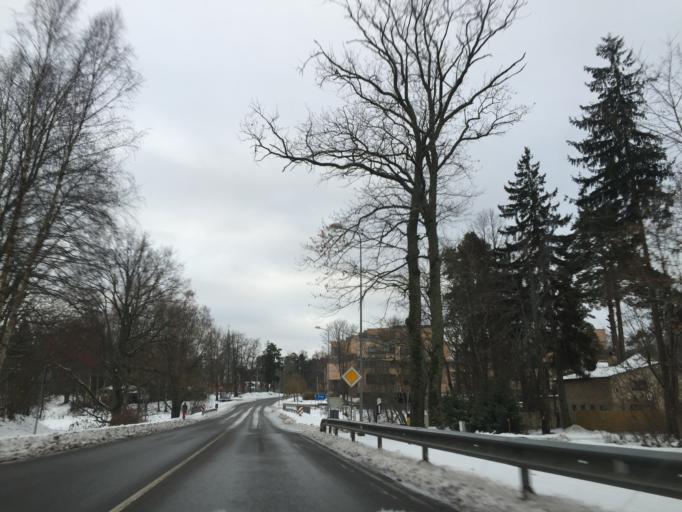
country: LV
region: Saulkrastu
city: Saulkrasti
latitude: 57.2788
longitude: 24.4169
